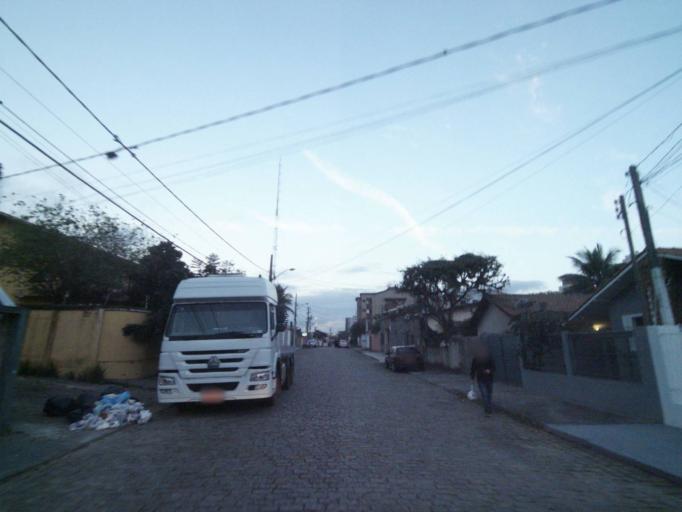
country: BR
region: Parana
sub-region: Paranagua
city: Paranagua
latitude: -25.5131
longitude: -48.5100
